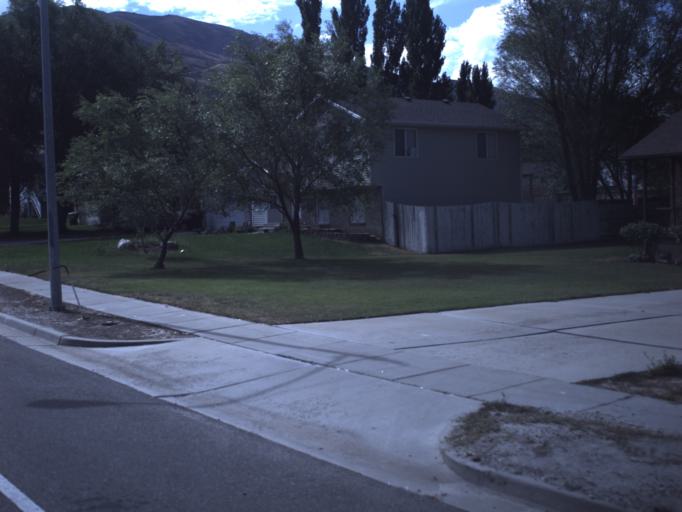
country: US
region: Utah
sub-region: Box Elder County
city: Brigham City
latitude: 41.5047
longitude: -112.0015
